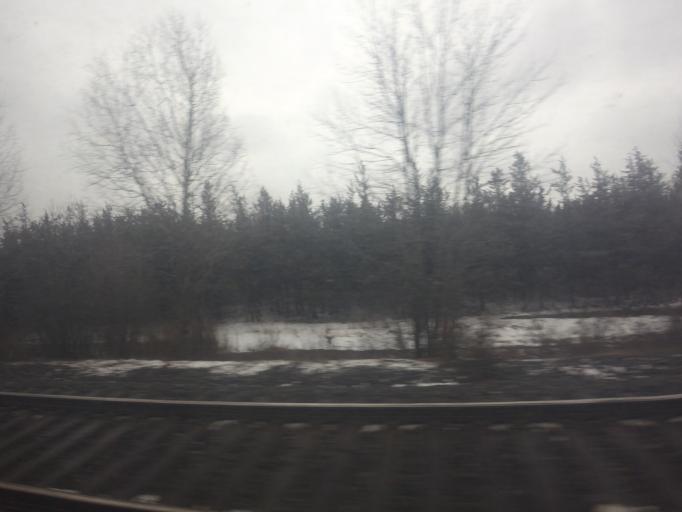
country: CA
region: Ontario
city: Belleville
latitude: 44.2029
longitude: -77.2426
